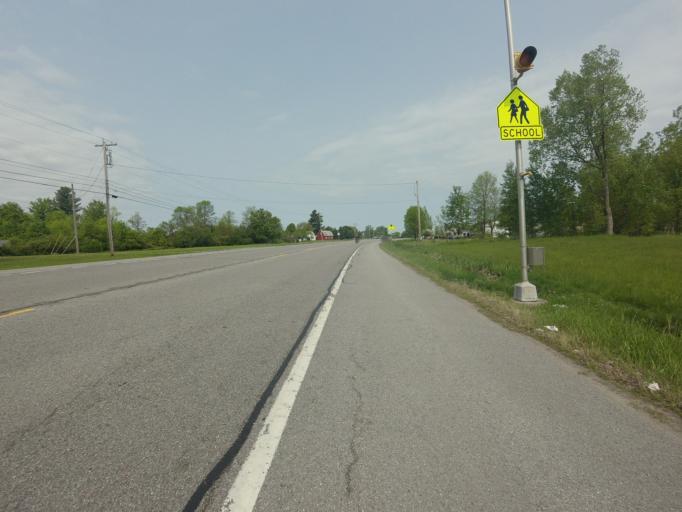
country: US
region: New York
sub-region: Jefferson County
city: Dexter
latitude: 44.0110
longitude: -76.0187
